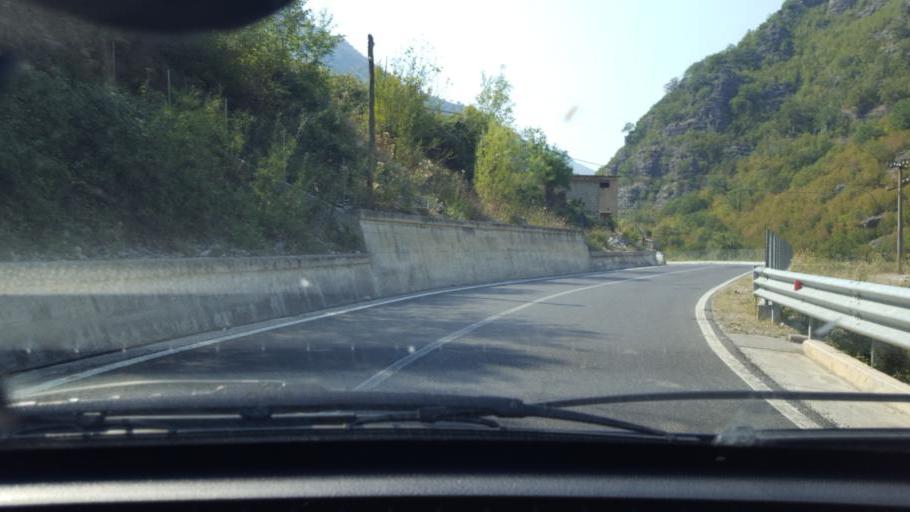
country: AL
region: Shkoder
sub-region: Rrethi i Malesia e Madhe
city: Kastrat
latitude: 42.4286
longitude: 19.5338
